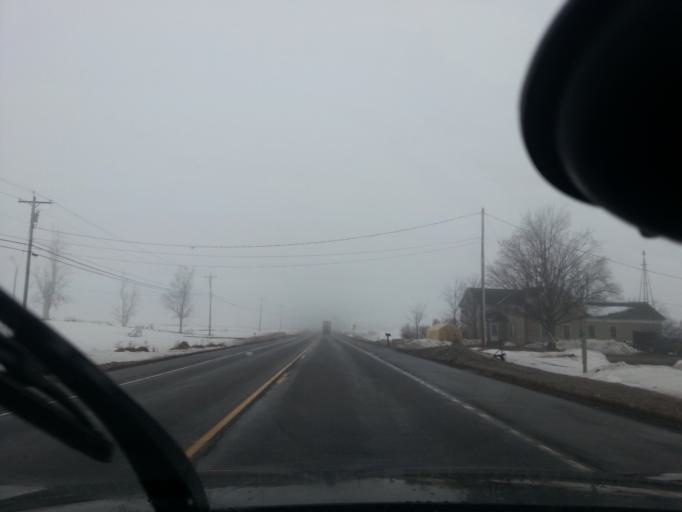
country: US
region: New York
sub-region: Jefferson County
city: Philadelphia
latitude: 44.1397
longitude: -75.7239
